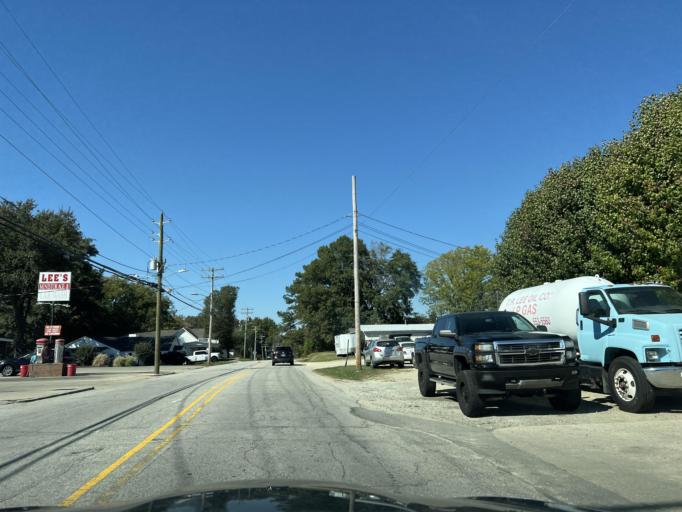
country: US
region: North Carolina
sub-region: Johnston County
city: Clayton
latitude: 35.6560
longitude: -78.4633
